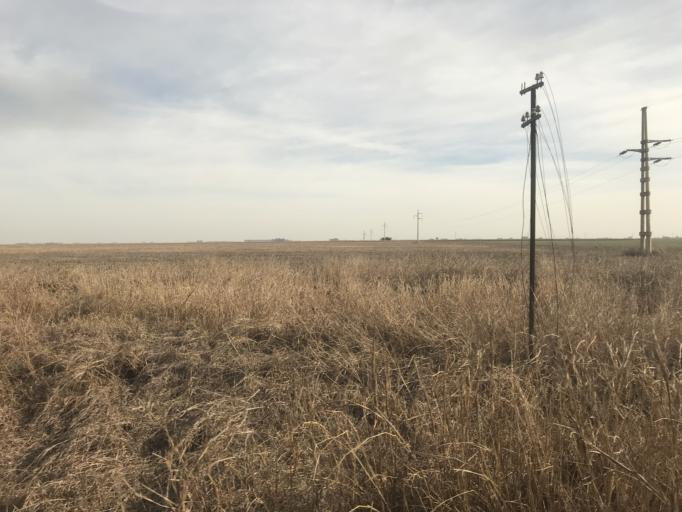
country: AR
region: Cordoba
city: Pilar
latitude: -31.6996
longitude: -63.8705
